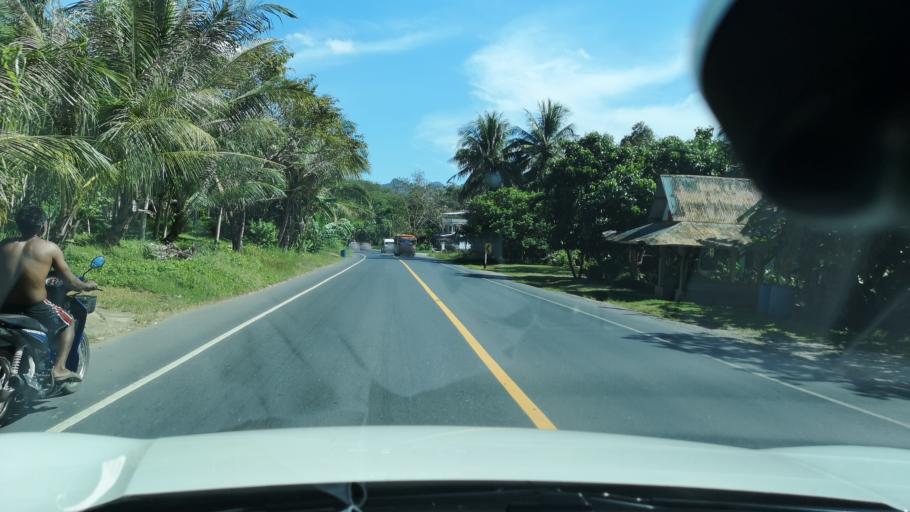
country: TH
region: Phangnga
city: Phang Nga
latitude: 8.5349
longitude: 98.5017
